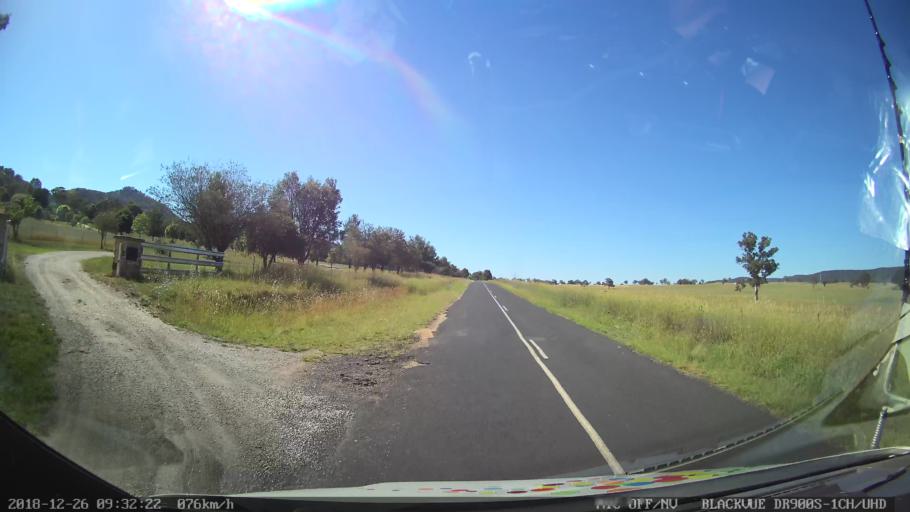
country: AU
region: New South Wales
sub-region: Mid-Western Regional
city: Kandos
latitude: -32.8837
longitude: 150.0323
